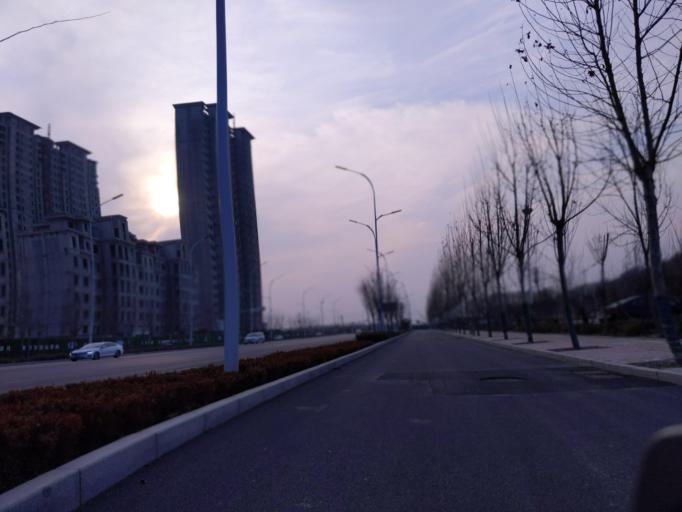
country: CN
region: Henan Sheng
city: Puyang
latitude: 35.8180
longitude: 115.0108
